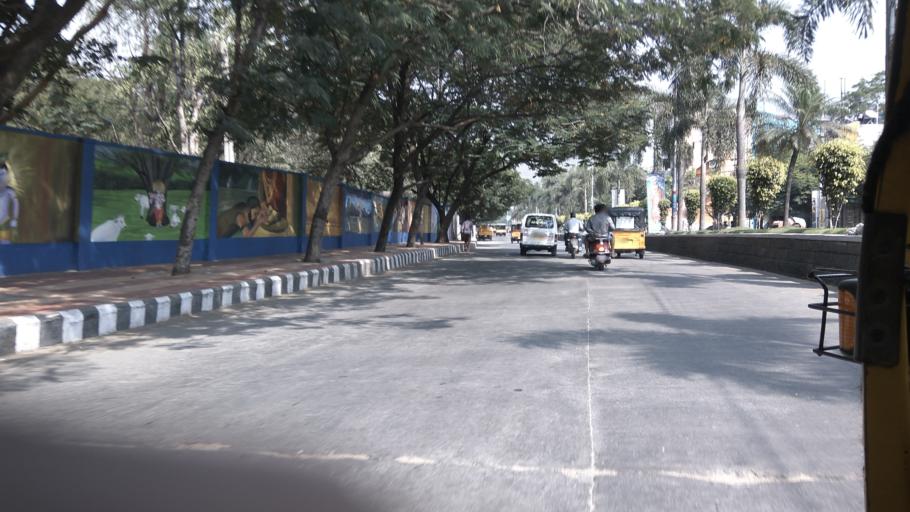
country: IN
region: Andhra Pradesh
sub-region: Chittoor
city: Tirupati
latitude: 13.6406
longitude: 79.4100
